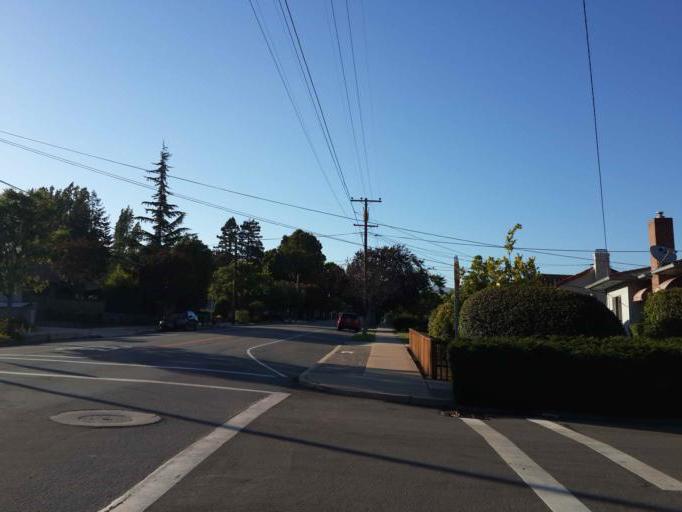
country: US
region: California
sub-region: San Luis Obispo County
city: San Luis Obispo
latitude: 35.2869
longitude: -120.6685
